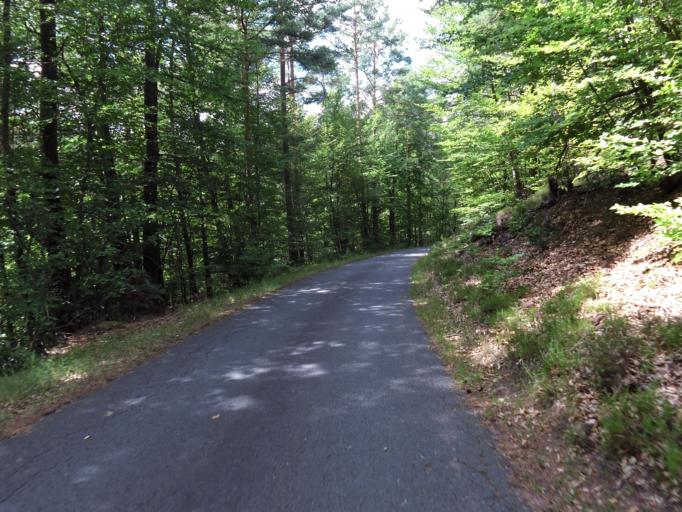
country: DE
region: Rheinland-Pfalz
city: Waldleiningen
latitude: 49.3951
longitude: 7.8980
